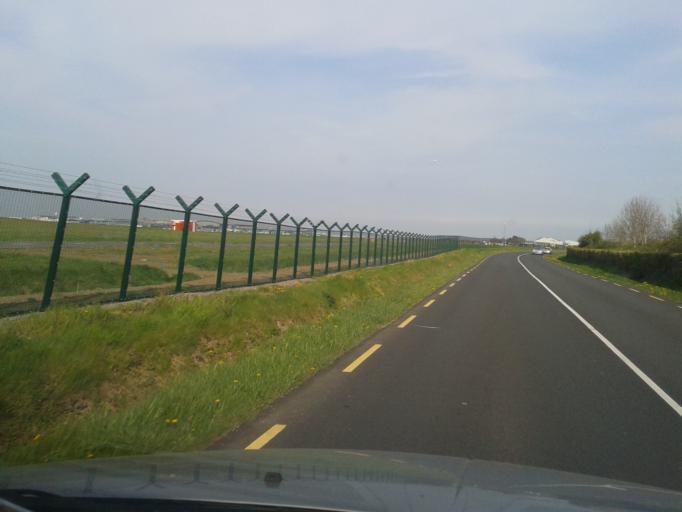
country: IE
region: Leinster
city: Ballymun
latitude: 53.4194
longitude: -6.2727
